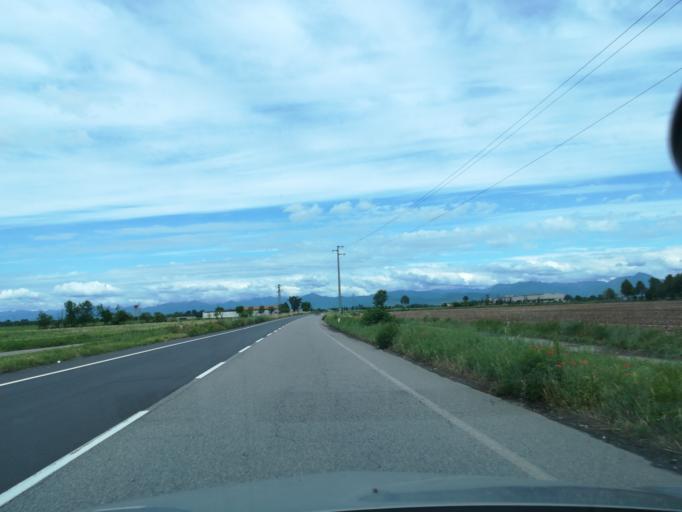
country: IT
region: Lombardy
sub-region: Provincia di Bergamo
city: Calcio
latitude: 45.5164
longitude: 9.8333
